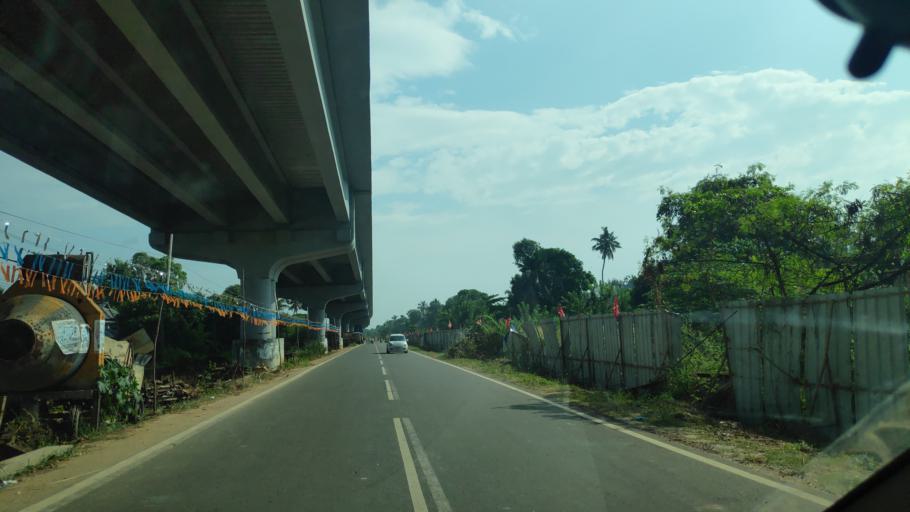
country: IN
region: Kerala
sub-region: Alappuzha
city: Alleppey
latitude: 9.4809
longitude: 76.3215
